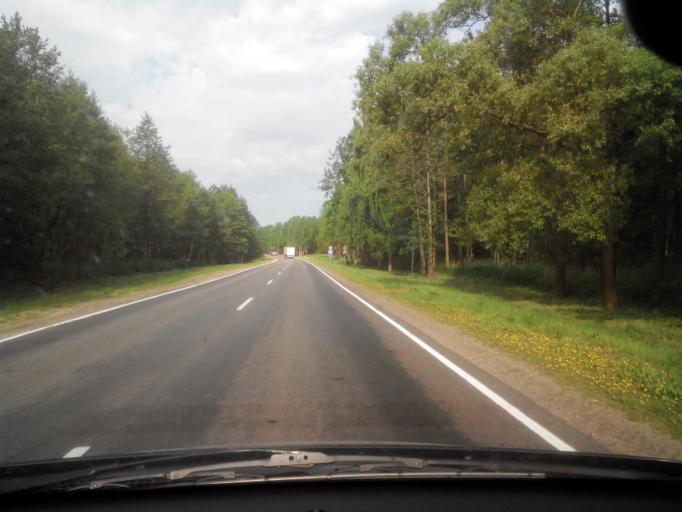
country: BY
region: Minsk
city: Myadzyel
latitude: 55.0618
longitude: 27.1537
